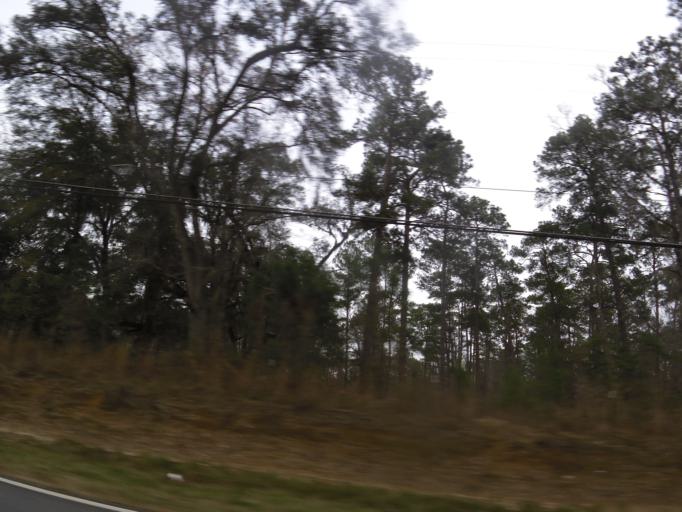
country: US
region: Georgia
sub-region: Thomas County
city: Thomasville
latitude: 30.8650
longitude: -84.0313
